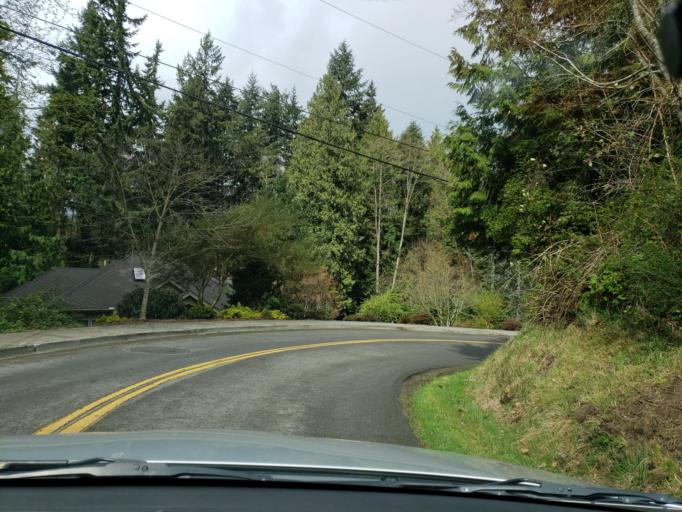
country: US
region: Washington
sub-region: Snohomish County
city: Meadowdale
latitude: 47.8338
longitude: -122.3338
